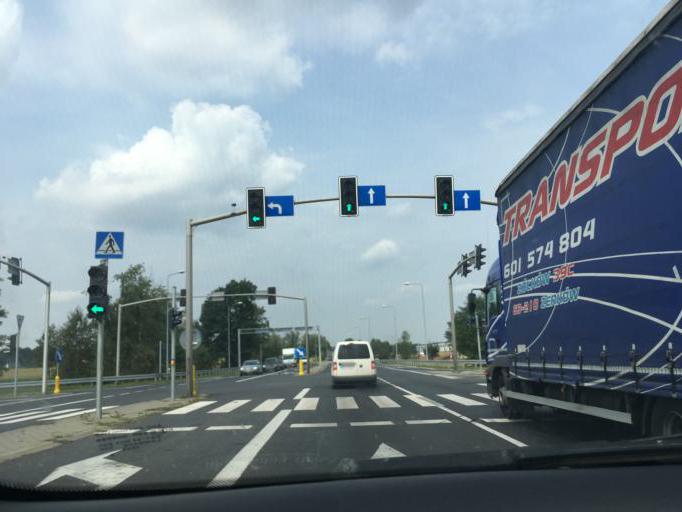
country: PL
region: Silesian Voivodeship
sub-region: Powiat bierunsko-ledzinski
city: Bierun
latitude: 50.0924
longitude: 19.1045
